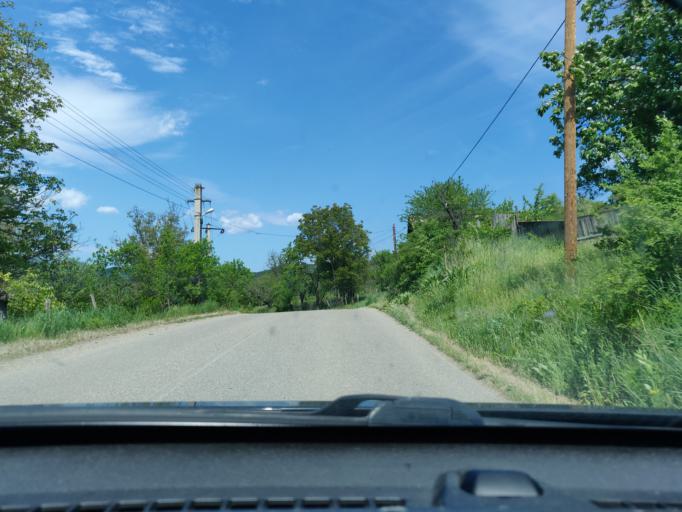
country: RO
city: Vizantea-Manastireasca
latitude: 45.9779
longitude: 26.8068
